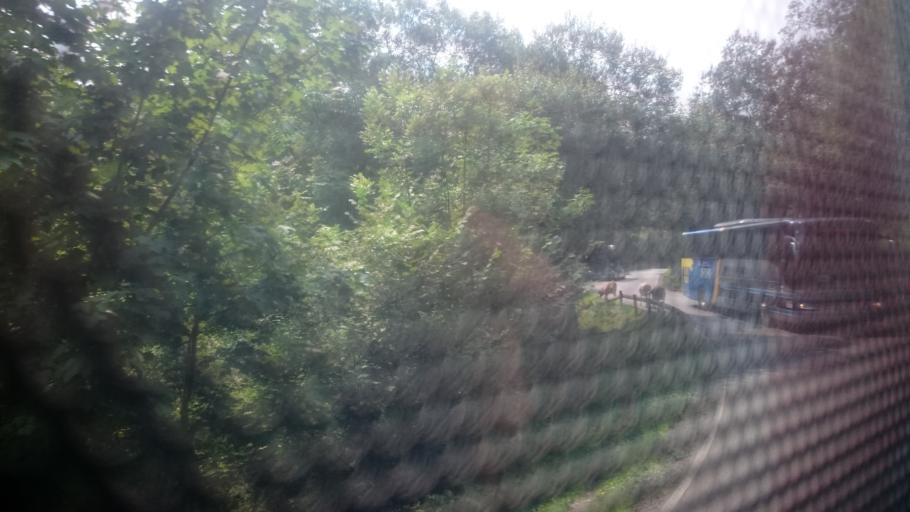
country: ES
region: Asturias
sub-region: Province of Asturias
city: Amieva
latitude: 43.2975
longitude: -5.0248
